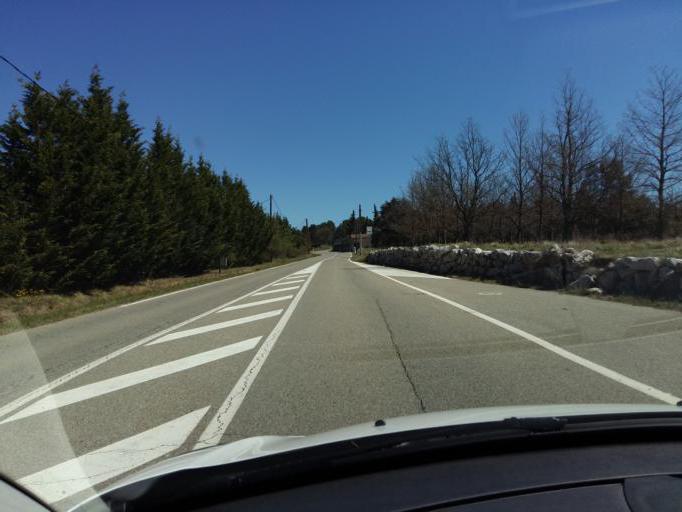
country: FR
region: Provence-Alpes-Cote d'Azur
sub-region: Departement du Vaucluse
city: Saignon
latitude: 43.9165
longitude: 5.4705
